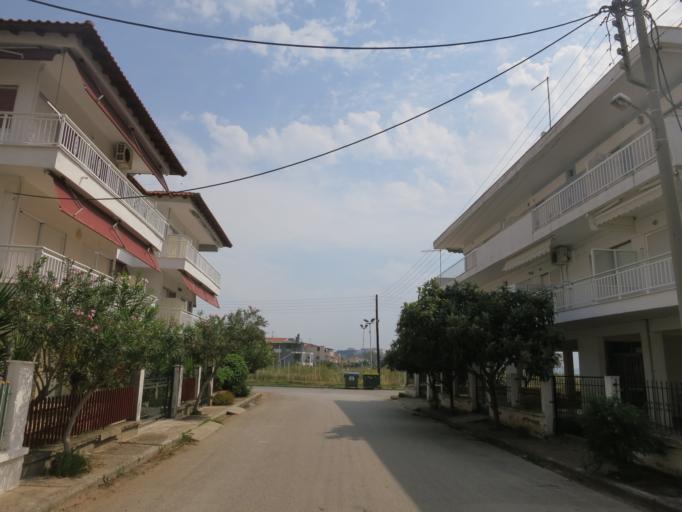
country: GR
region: Central Macedonia
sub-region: Nomos Chalkidikis
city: Nea Moudhania
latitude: 40.2493
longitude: 23.2533
